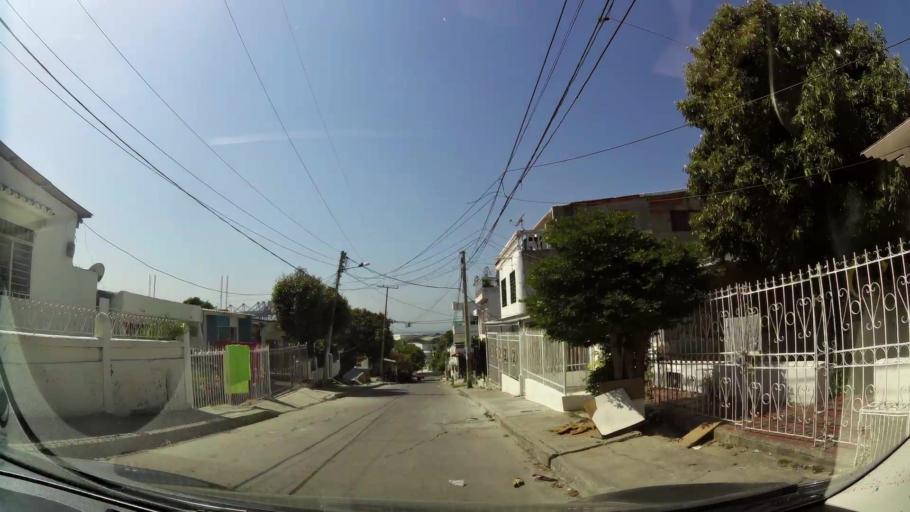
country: CO
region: Bolivar
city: Cartagena
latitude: 10.3910
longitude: -75.5115
